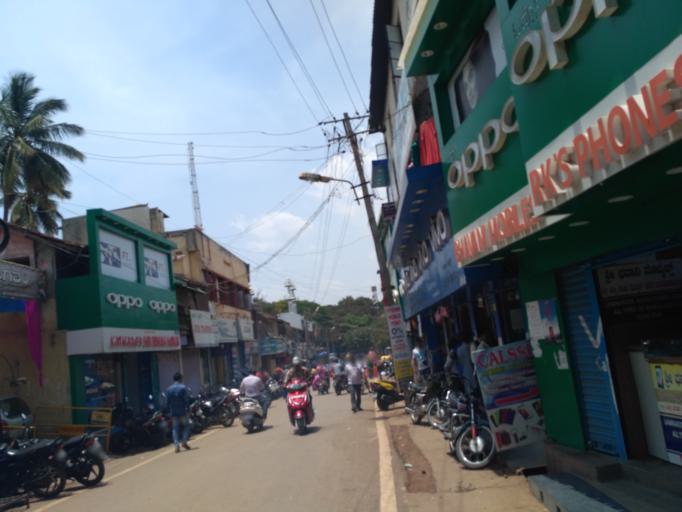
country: IN
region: Karnataka
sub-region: Dharwad
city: Hubli
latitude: 15.4581
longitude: 75.0118
